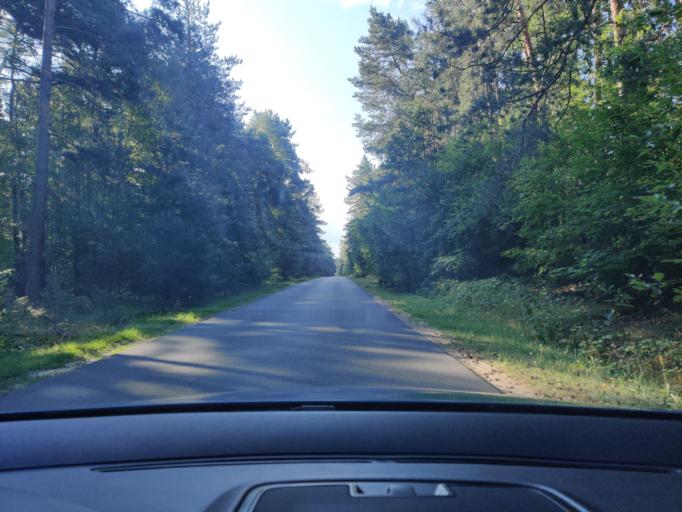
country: PL
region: Greater Poland Voivodeship
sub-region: Konin
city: Konin
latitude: 52.1819
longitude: 18.3330
